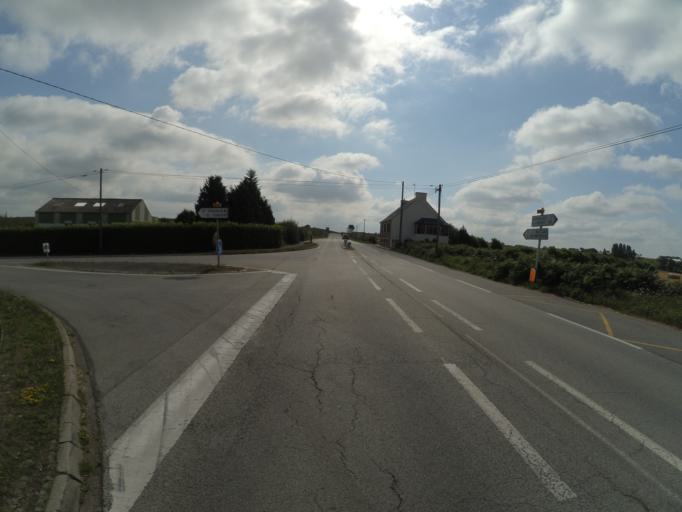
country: FR
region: Brittany
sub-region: Departement du Finistere
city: Le Trevoux
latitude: 47.9171
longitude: -3.6143
